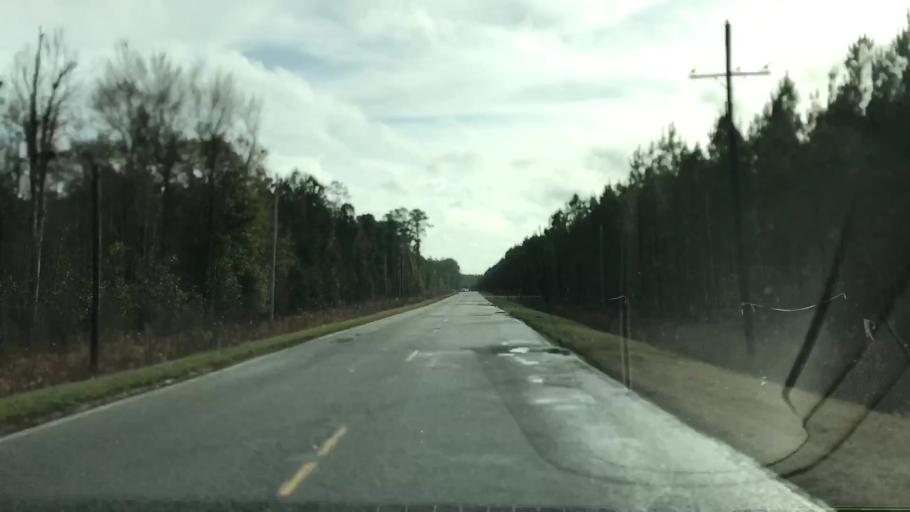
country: US
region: South Carolina
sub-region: Williamsburg County
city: Andrews
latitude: 33.4305
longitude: -79.5939
